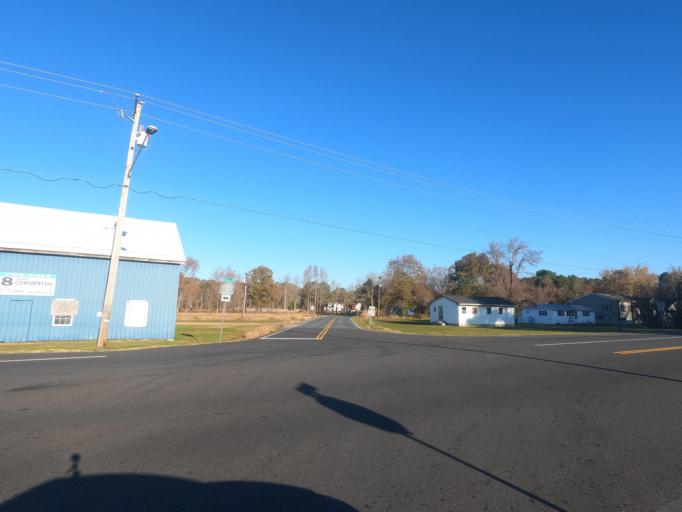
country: US
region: Maryland
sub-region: Somerset County
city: Crisfield
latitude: 38.0101
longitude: -75.8155
